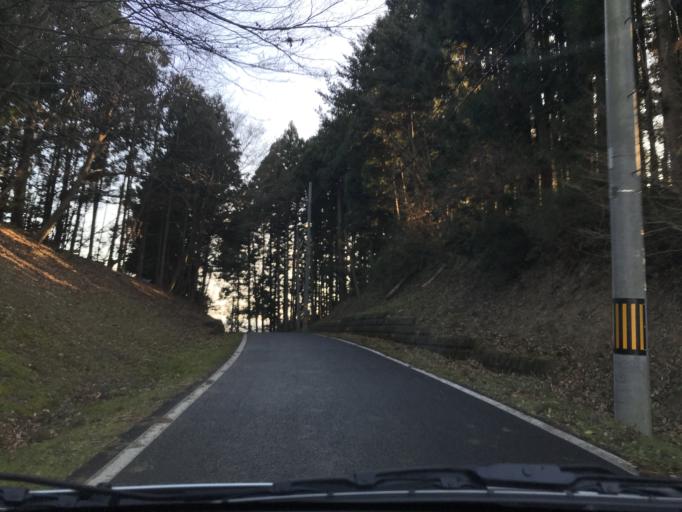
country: JP
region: Miyagi
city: Wakuya
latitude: 38.6853
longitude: 141.1122
